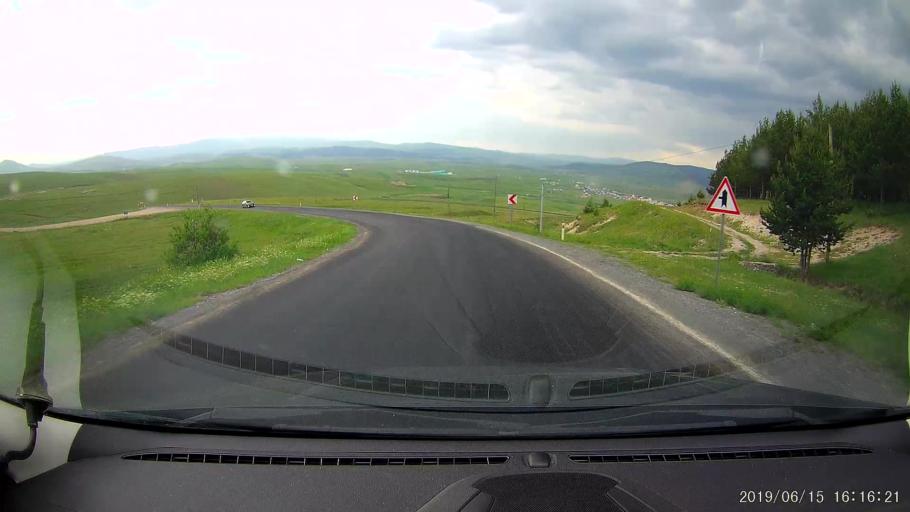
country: TR
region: Ardahan
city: Hanak
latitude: 41.2593
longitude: 42.8524
